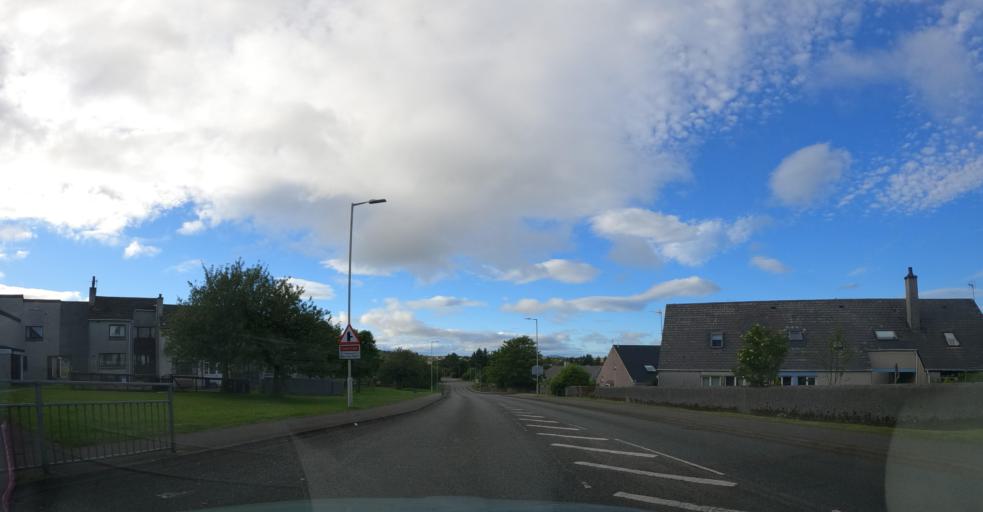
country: GB
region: Scotland
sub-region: Eilean Siar
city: Isle of Lewis
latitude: 58.2219
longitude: -6.3862
